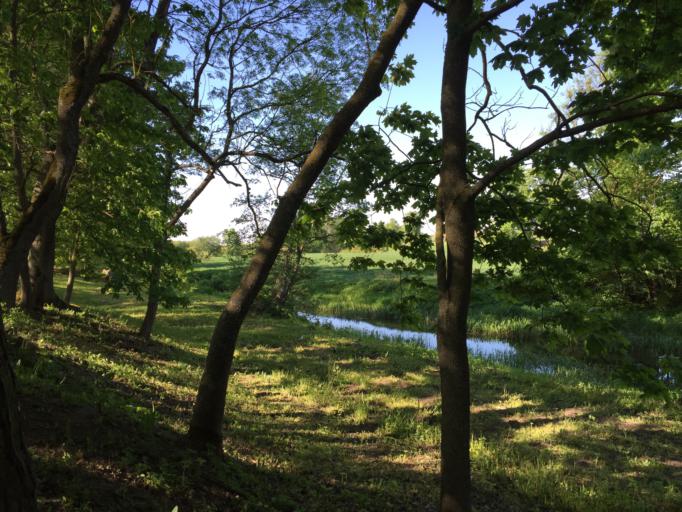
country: LV
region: Jelgava
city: Jelgava
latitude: 56.5213
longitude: 23.7581
